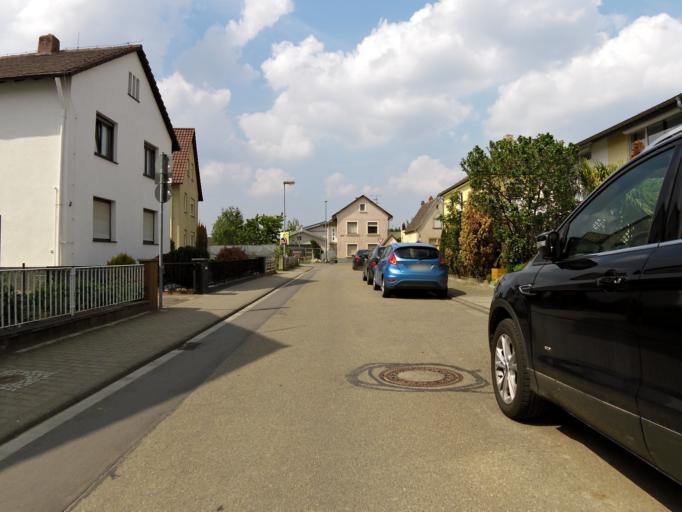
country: DE
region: Rheinland-Pfalz
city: Hochdorf-Assenheim
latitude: 49.4141
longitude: 8.2680
